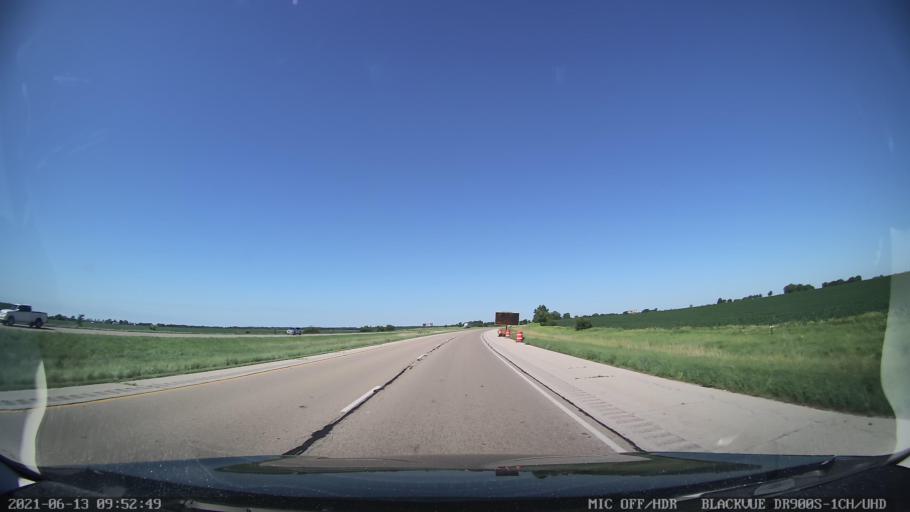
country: US
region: Illinois
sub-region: McLean County
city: Twin Grove
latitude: 40.3978
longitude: -89.0633
